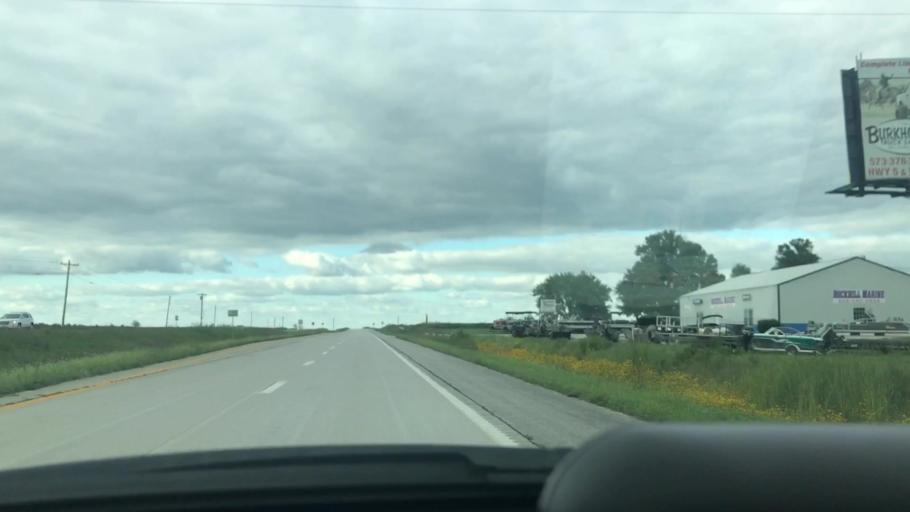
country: US
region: Missouri
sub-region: Benton County
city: Lincoln
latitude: 38.3526
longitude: -93.3394
